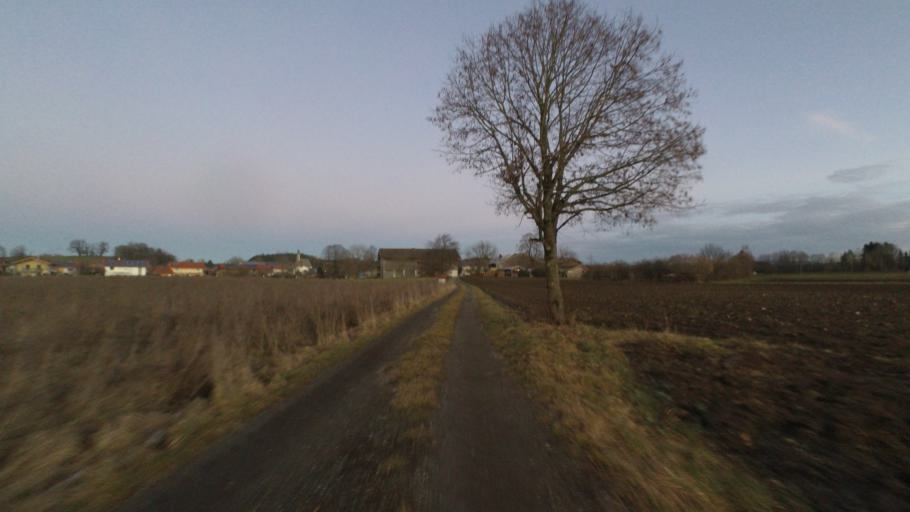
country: DE
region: Bavaria
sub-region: Upper Bavaria
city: Chieming
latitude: 47.9101
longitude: 12.5558
